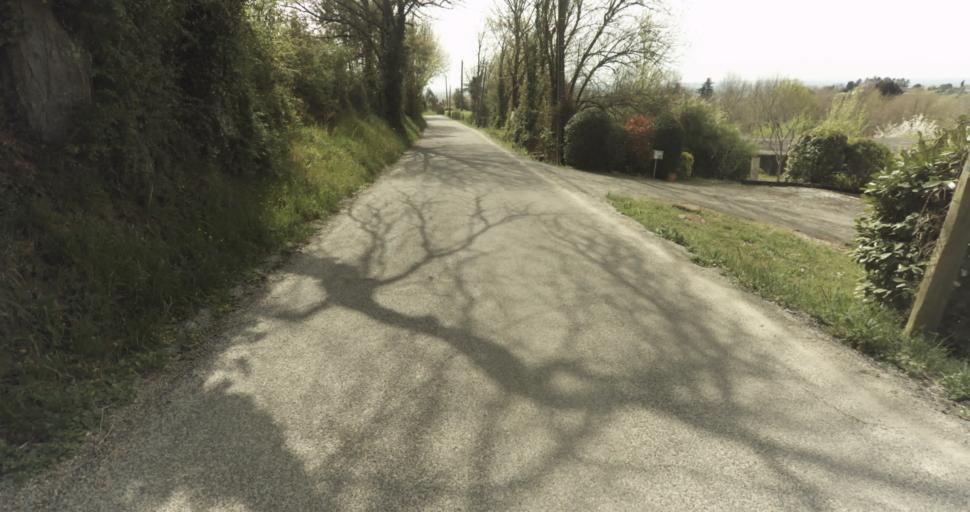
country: FR
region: Midi-Pyrenees
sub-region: Departement du Tarn-et-Garonne
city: Moissac
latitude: 44.1118
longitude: 1.0851
